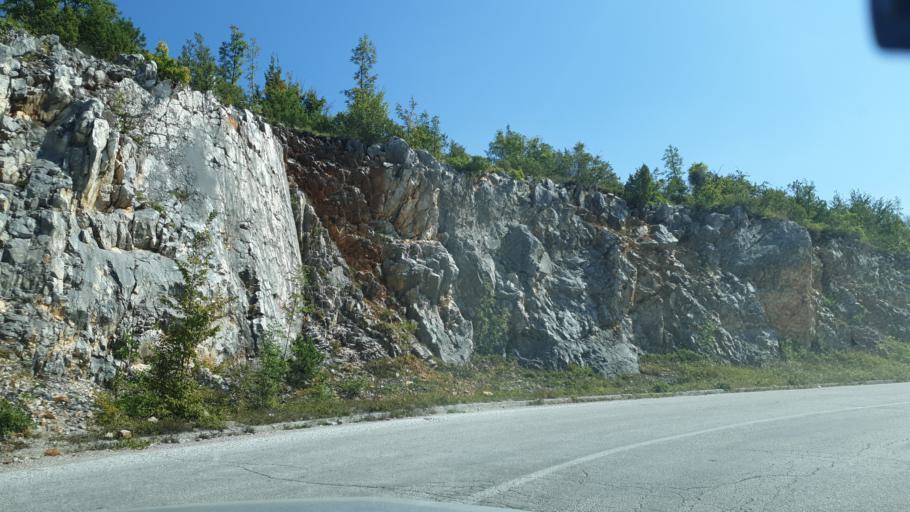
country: RS
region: Central Serbia
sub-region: Zlatiborski Okrug
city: Cajetina
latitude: 43.6827
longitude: 19.8510
